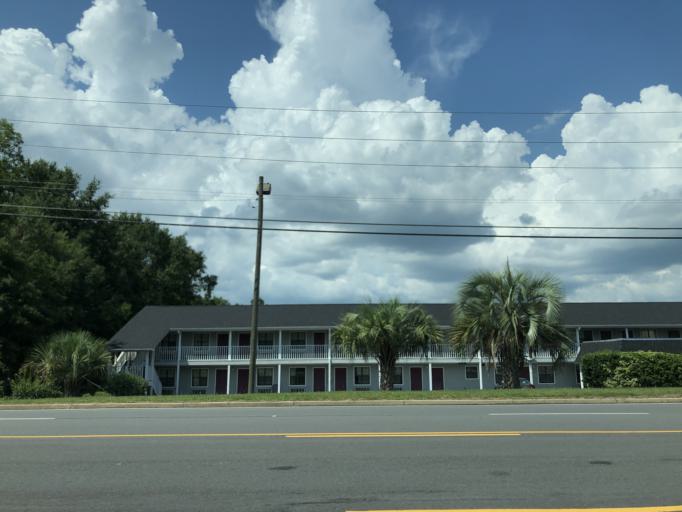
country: US
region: Georgia
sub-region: Telfair County
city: McRae
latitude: 32.0635
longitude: -82.8862
